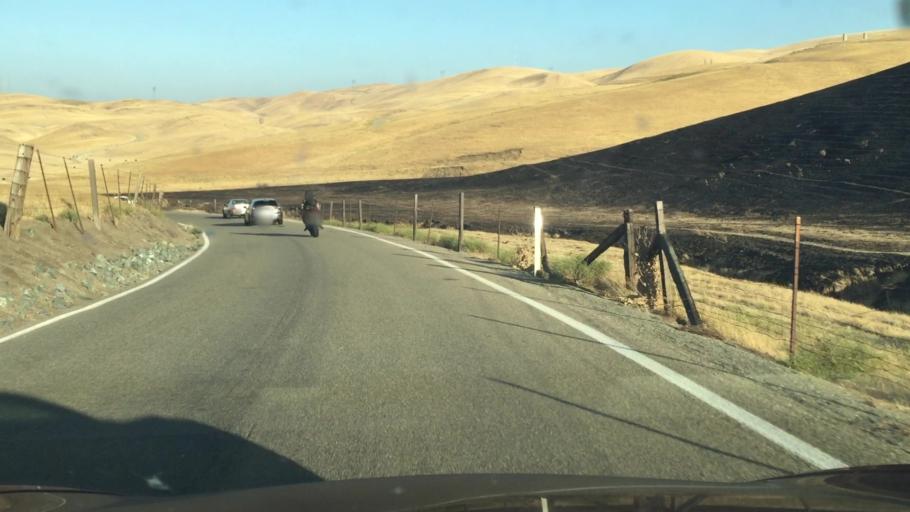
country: US
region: California
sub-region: San Joaquin County
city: Mountain House
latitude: 37.6866
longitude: -121.6032
